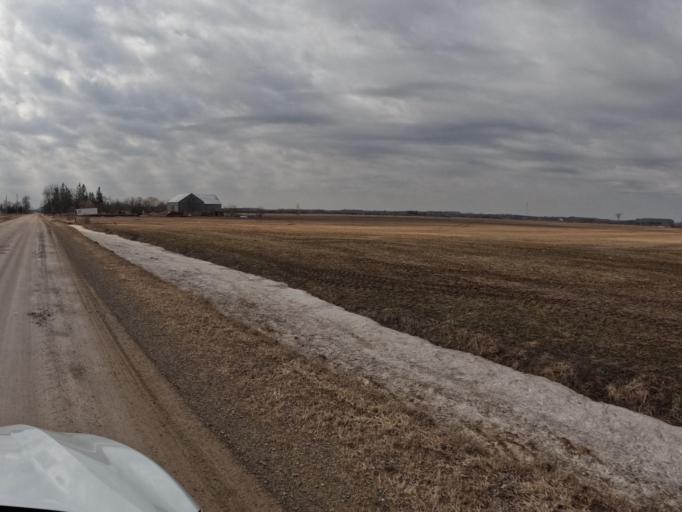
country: CA
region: Ontario
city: Orangeville
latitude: 43.9148
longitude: -80.2166
